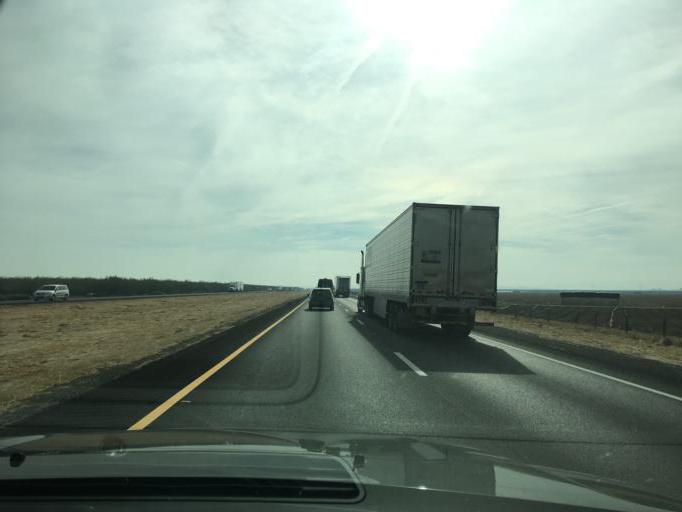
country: US
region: California
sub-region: Fresno County
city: Huron
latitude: 36.1968
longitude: -120.2079
